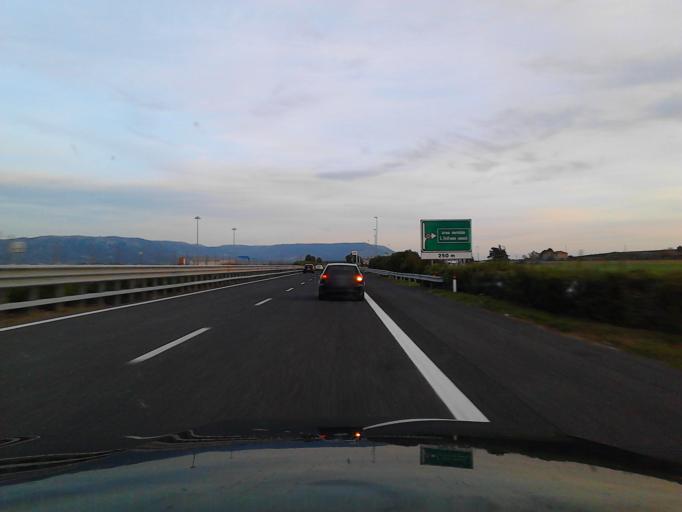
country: IT
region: Apulia
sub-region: Provincia di Foggia
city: Poggio Imperiale
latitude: 41.7825
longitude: 15.3813
